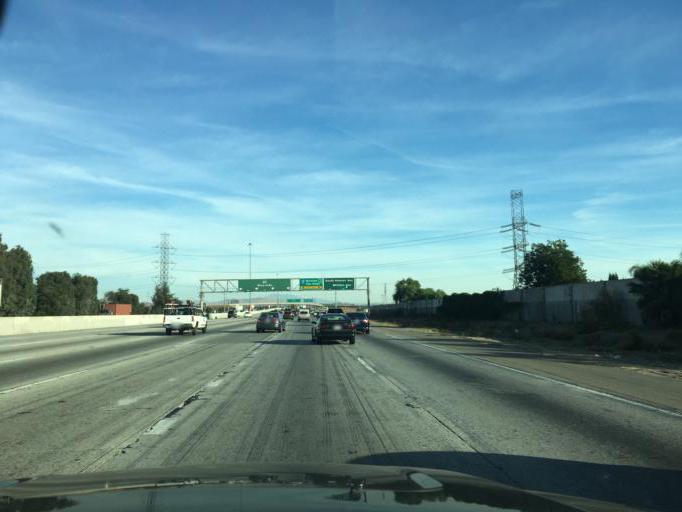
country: US
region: California
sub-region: Riverside County
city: Mira Loma
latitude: 34.0257
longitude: -117.5651
